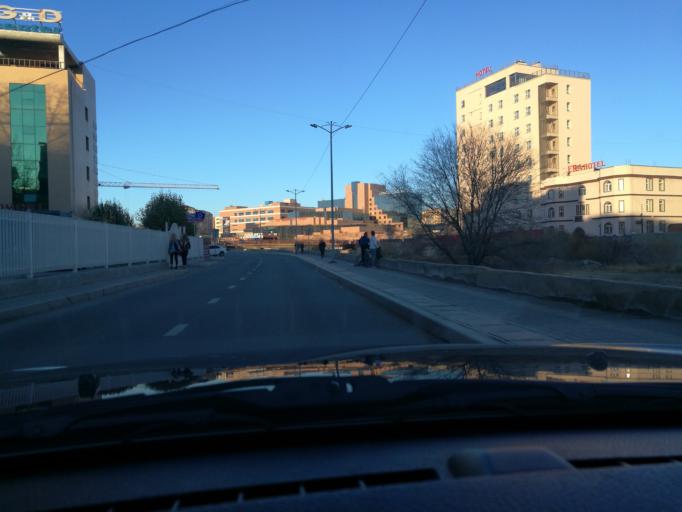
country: MN
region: Ulaanbaatar
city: Ulaanbaatar
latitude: 47.9197
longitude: 106.9301
